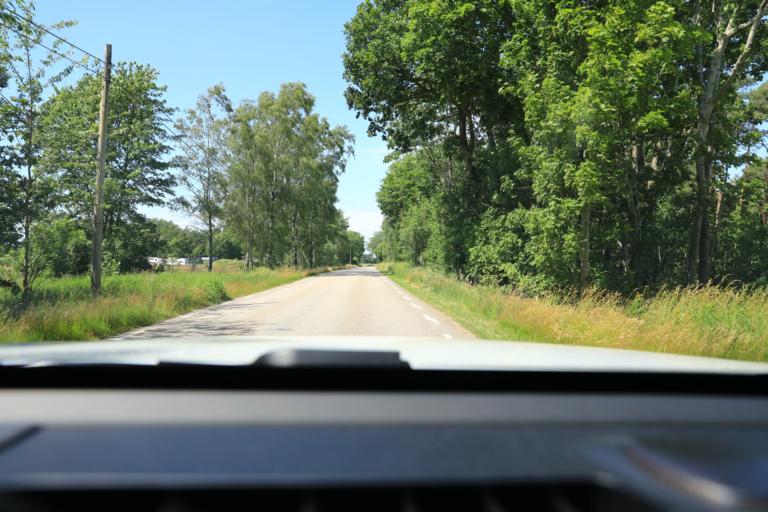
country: SE
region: Halland
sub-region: Varbergs Kommun
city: Tvaaker
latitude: 57.0943
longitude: 12.3964
